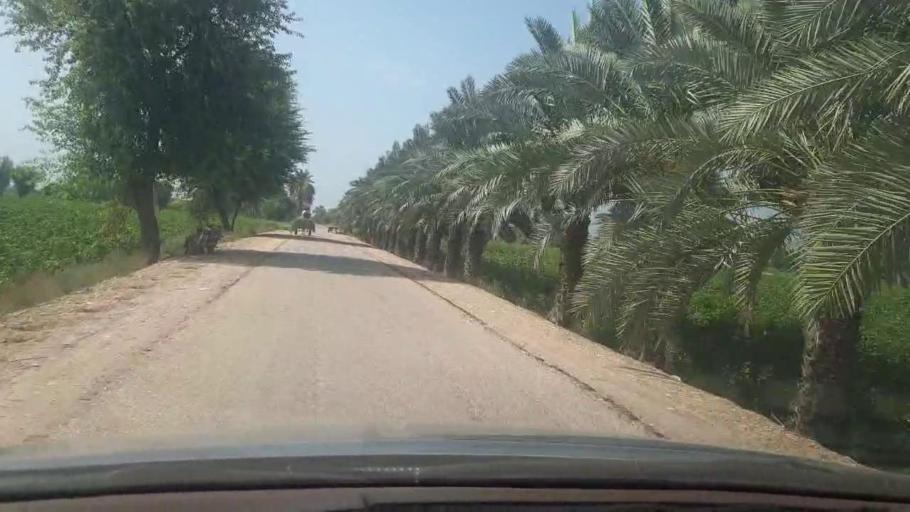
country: PK
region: Sindh
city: Ranipur
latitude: 27.2794
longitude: 68.5816
